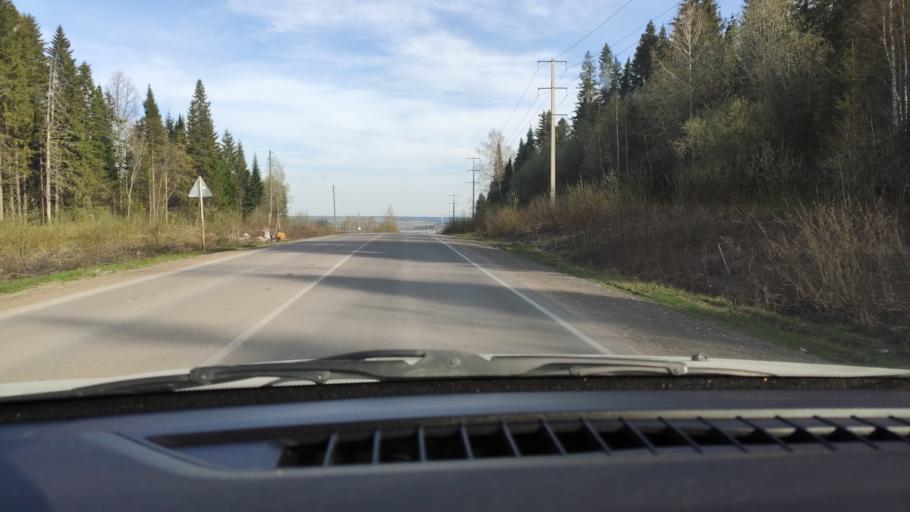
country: RU
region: Perm
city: Novyye Lyady
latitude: 57.9199
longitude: 56.6636
